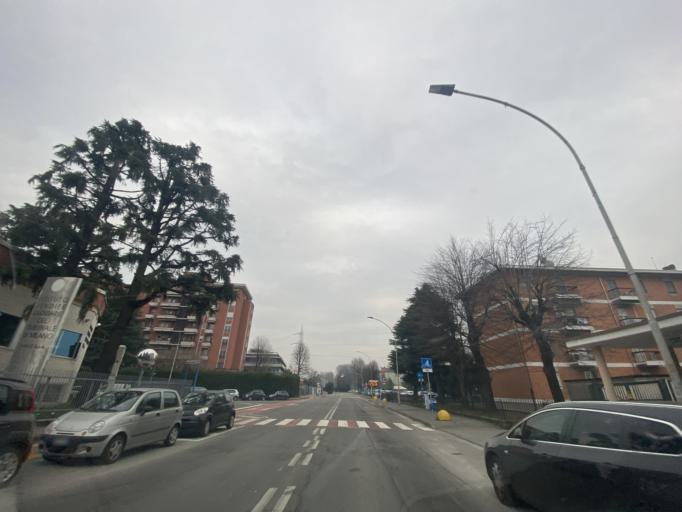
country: IT
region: Lombardy
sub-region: Citta metropolitana di Milano
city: Novegro-Tregarezzo-San Felice
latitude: 45.4801
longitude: 9.2673
